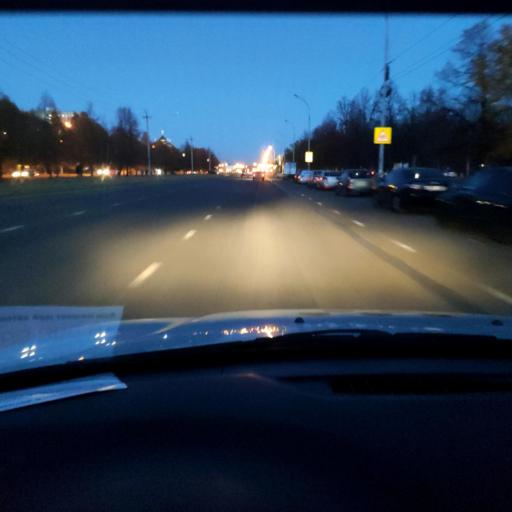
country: RU
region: Samara
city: Tol'yatti
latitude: 53.5208
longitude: 49.2659
